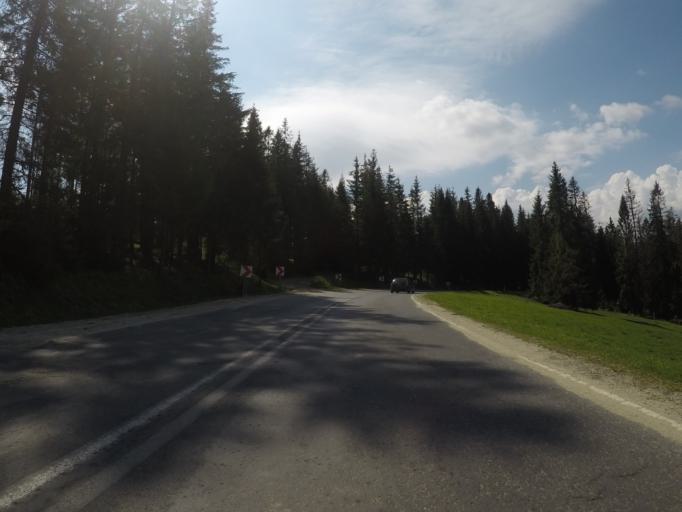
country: PL
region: Lesser Poland Voivodeship
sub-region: Powiat tatrzanski
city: Bukowina Tatrzanska
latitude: 49.3042
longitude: 20.1156
